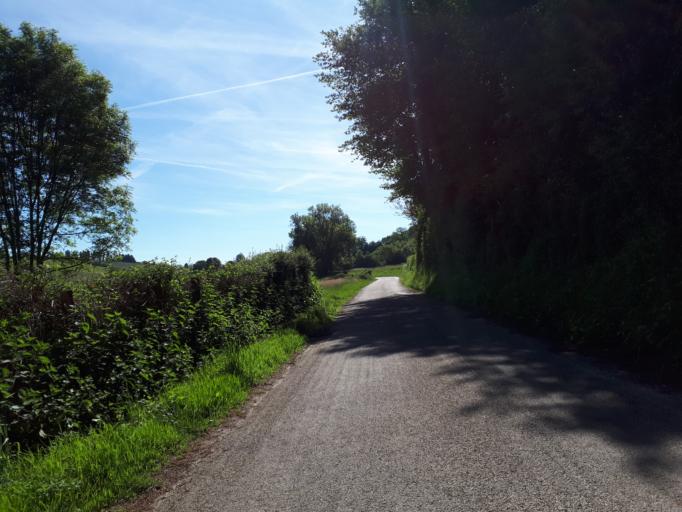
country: FR
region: Rhone-Alpes
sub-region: Departement de l'Isere
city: Saint-Savin
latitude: 45.6120
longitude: 5.3043
